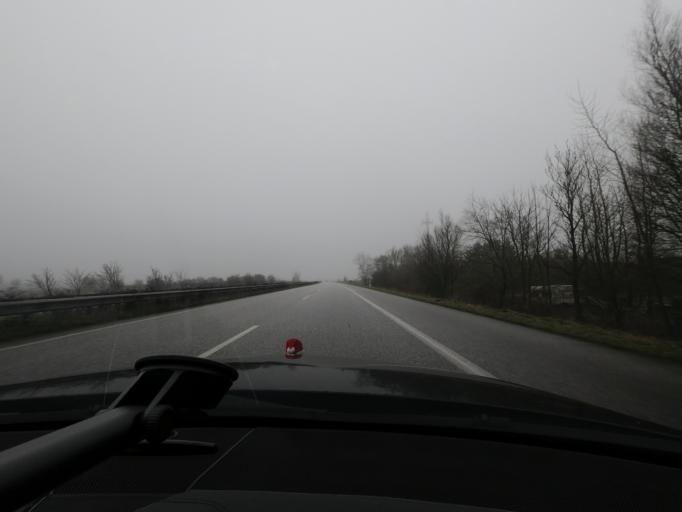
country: DE
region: Schleswig-Holstein
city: Sankelmark
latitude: 54.7002
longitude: 9.4038
